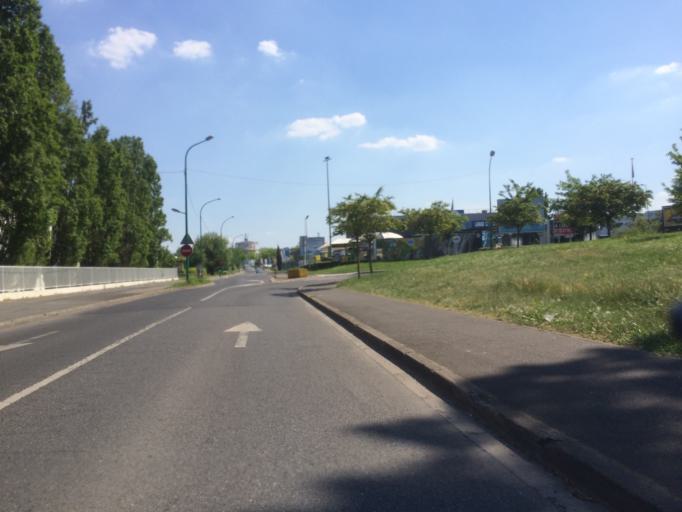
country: FR
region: Ile-de-France
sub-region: Departement de l'Essonne
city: Morangis
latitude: 48.6949
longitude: 2.3366
